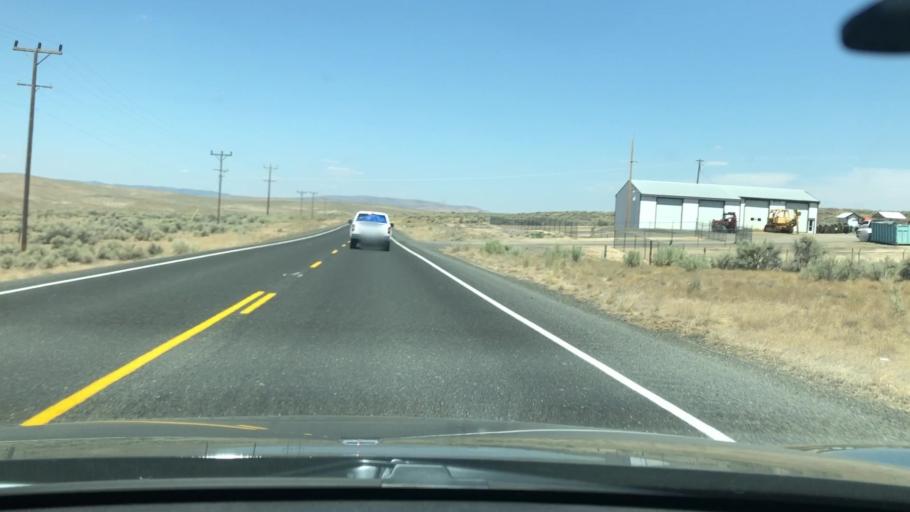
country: US
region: Idaho
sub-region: Owyhee County
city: Murphy
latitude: 43.0012
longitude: -117.0642
